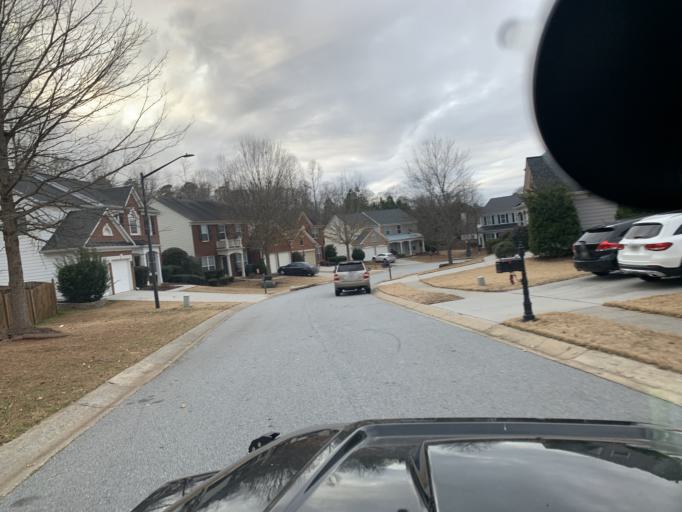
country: US
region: Georgia
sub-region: Cherokee County
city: Woodstock
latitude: 34.0979
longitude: -84.4595
